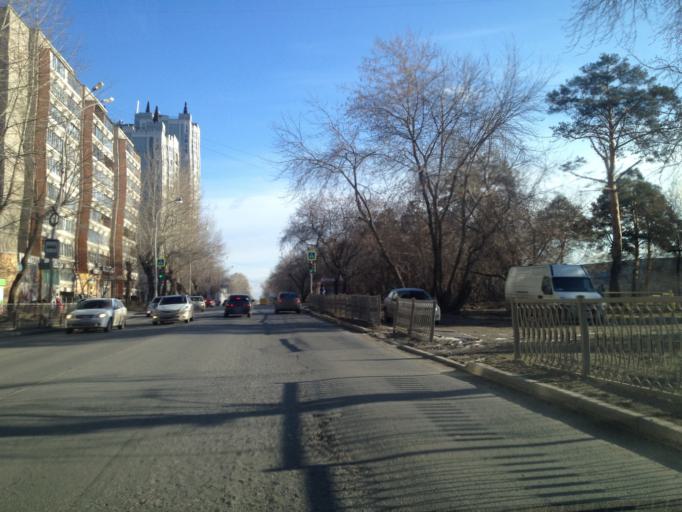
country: RU
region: Sverdlovsk
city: Sovkhoznyy
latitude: 56.7613
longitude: 60.6119
